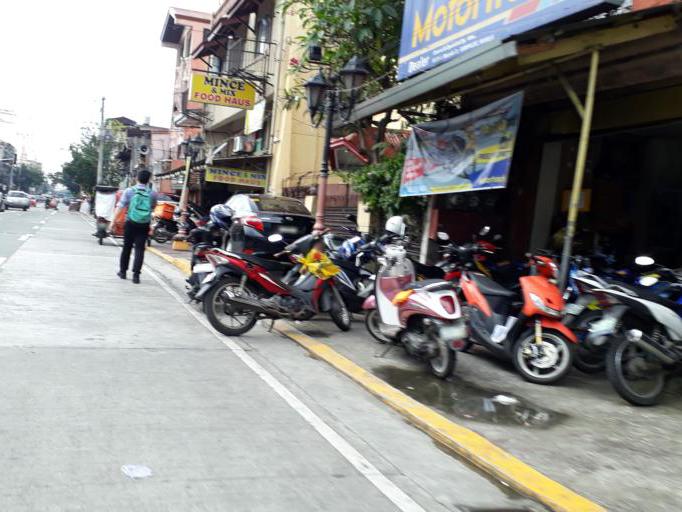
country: PH
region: Metro Manila
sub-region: City of Manila
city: Manila
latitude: 14.6168
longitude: 120.9957
